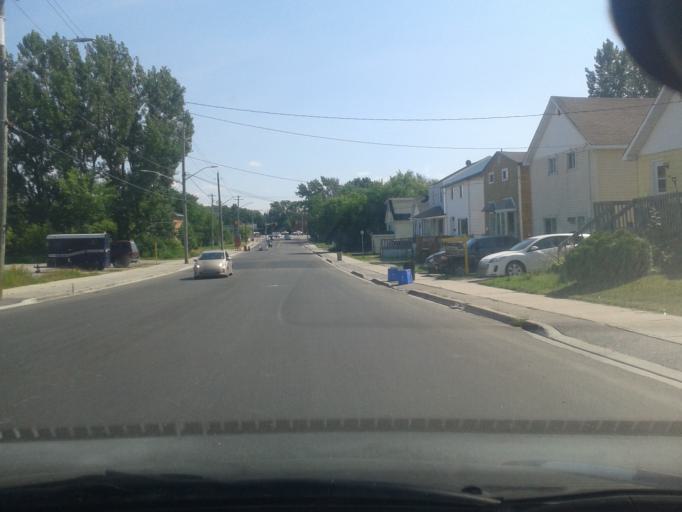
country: CA
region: Ontario
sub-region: Nipissing District
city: North Bay
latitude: 46.3136
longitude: -79.4497
